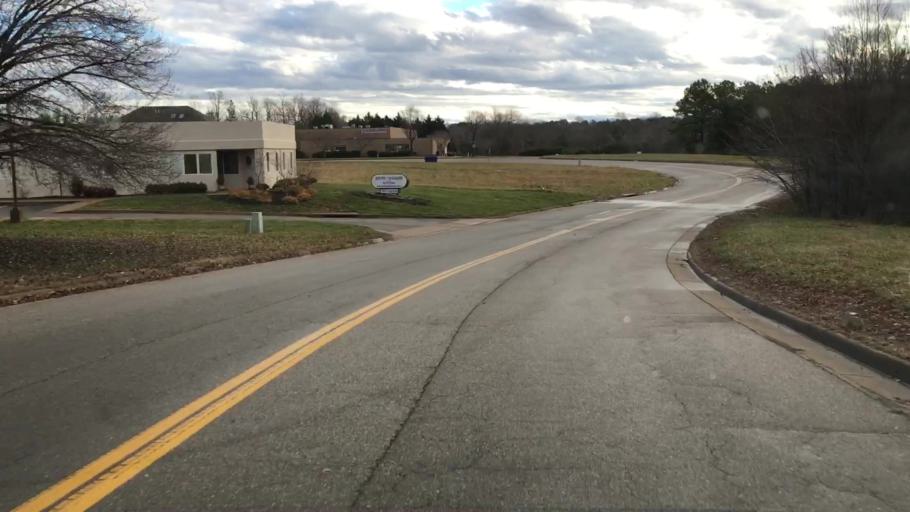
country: US
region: Virginia
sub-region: Chesterfield County
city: Bon Air
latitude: 37.5002
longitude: -77.5929
